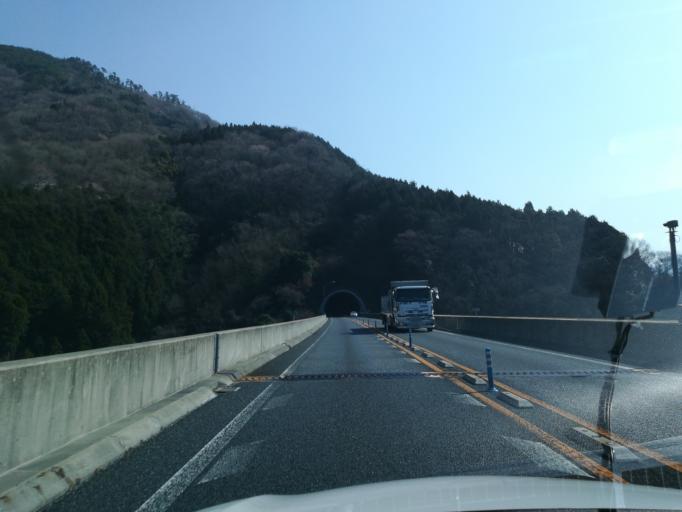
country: JP
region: Tokushima
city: Ikedacho
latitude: 34.0154
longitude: 133.7516
